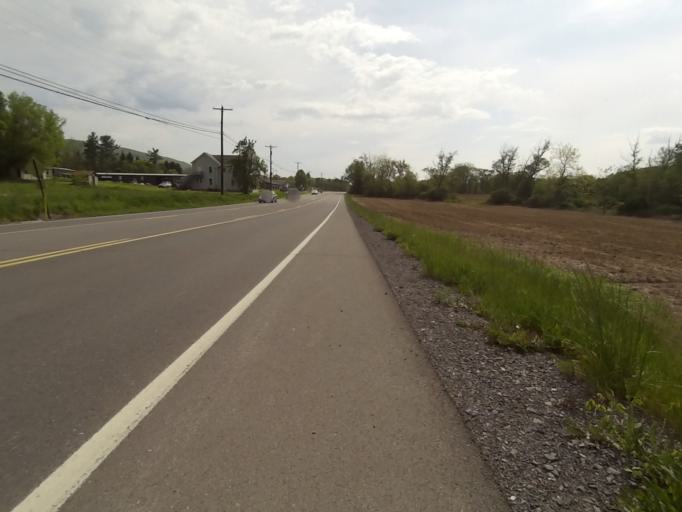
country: US
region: Pennsylvania
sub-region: Centre County
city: Pleasant Gap
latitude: 40.8598
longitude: -77.7592
